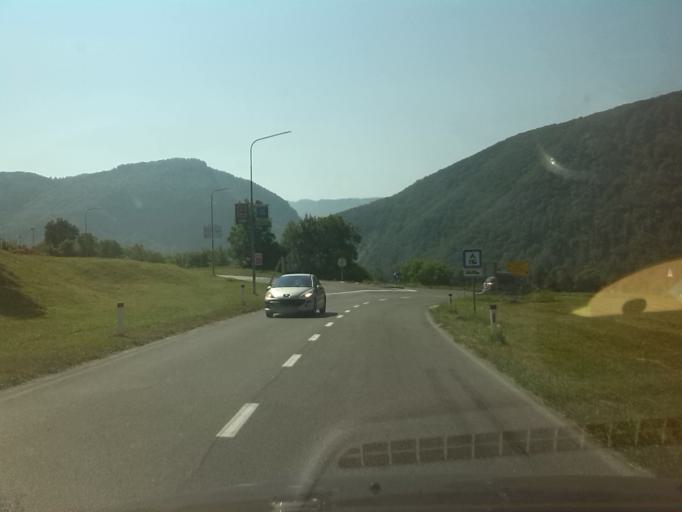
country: SI
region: Tolmin
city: Tolmin
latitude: 46.1813
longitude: 13.7404
